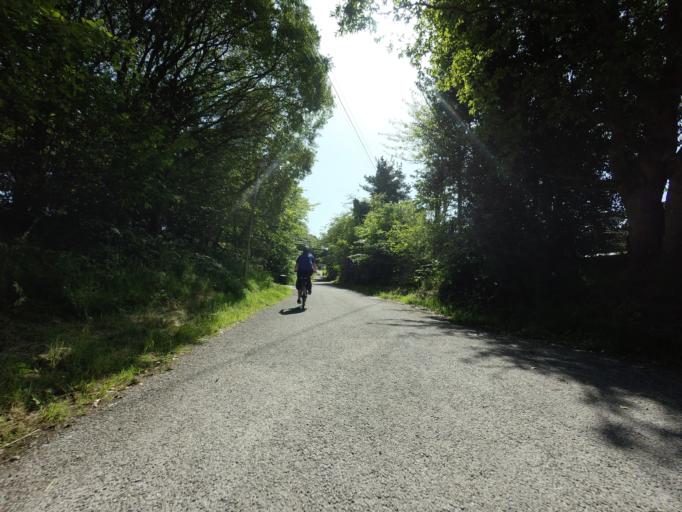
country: GB
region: Scotland
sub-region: Highland
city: Inverness
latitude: 57.4764
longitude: -4.1595
